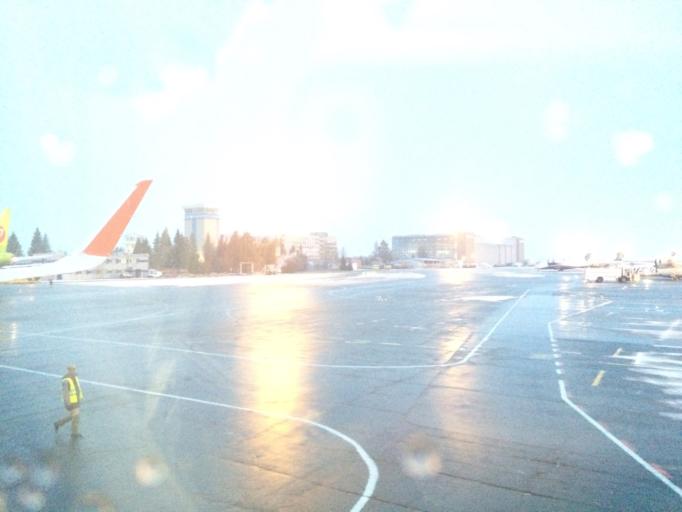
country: RU
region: Novosibirsk
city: Ob'
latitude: 55.0109
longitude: 82.6655
